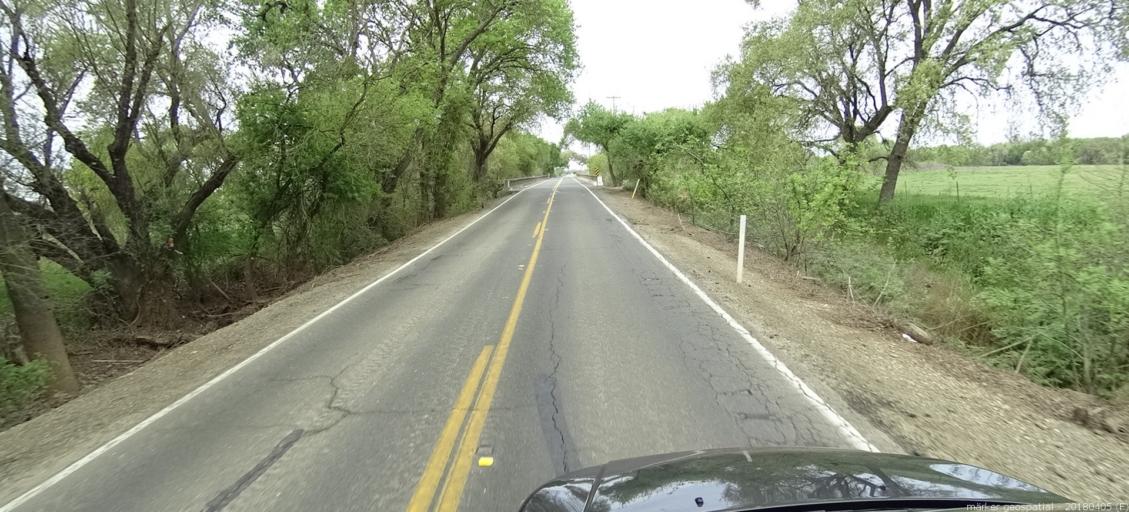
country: US
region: California
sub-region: San Joaquin County
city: Thornton
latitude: 38.2413
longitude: -121.3840
